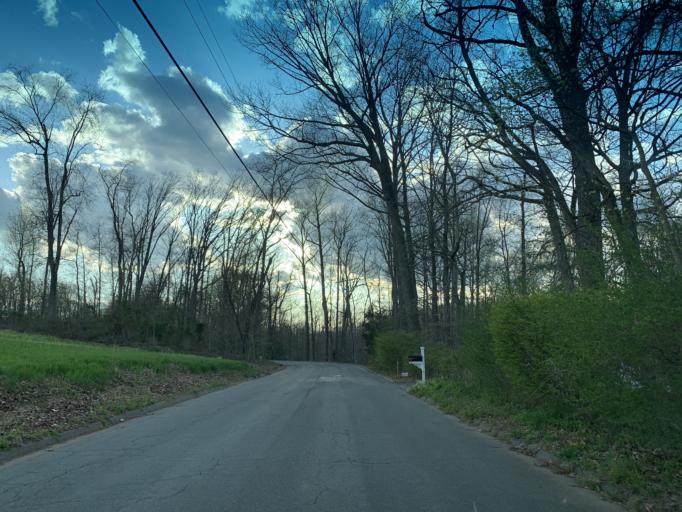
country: US
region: Maryland
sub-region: Harford County
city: South Bel Air
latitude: 39.6110
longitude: -76.2921
